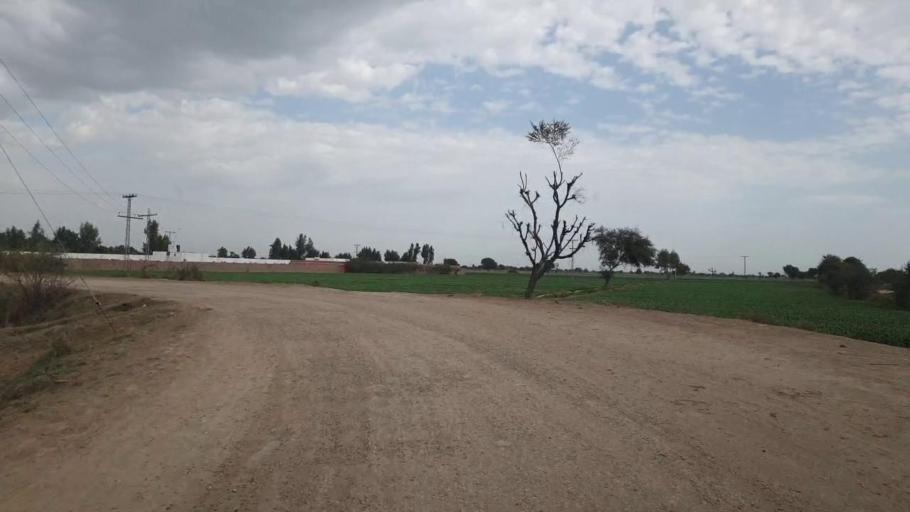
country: PK
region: Sindh
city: Hala
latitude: 25.9283
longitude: 68.3891
